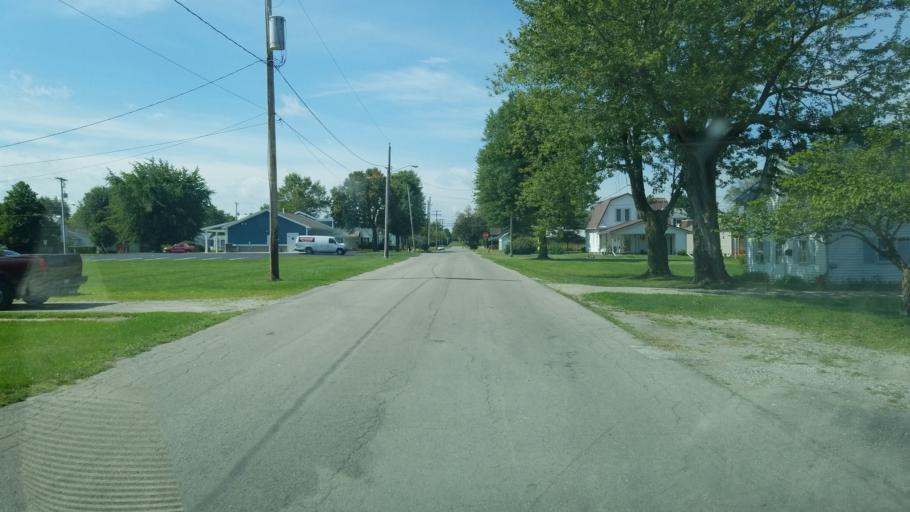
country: US
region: Ohio
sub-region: Hardin County
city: Kenton
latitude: 40.6380
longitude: -83.6035
